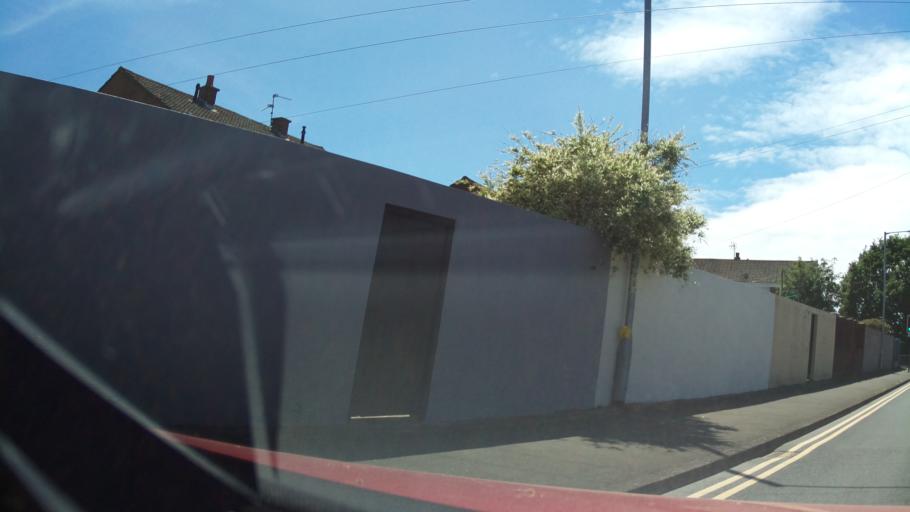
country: GB
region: Wales
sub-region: Monmouthshire
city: Caldicot
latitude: 51.5872
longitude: -2.7565
